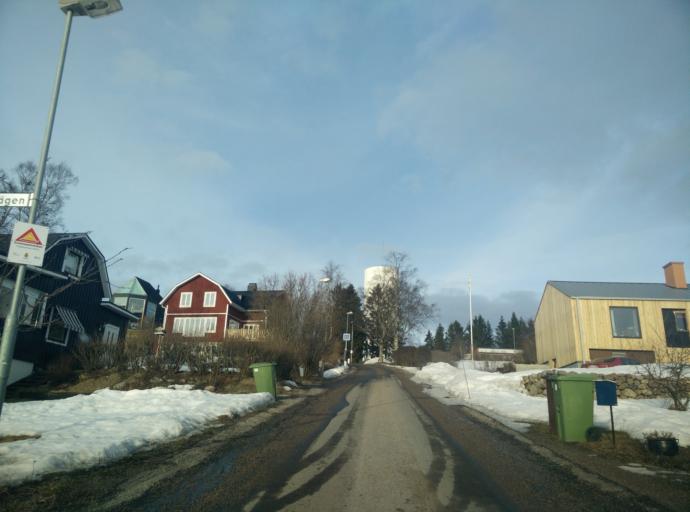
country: SE
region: Vaesternorrland
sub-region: Sundsvalls Kommun
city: Johannedal
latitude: 62.4337
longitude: 17.4189
